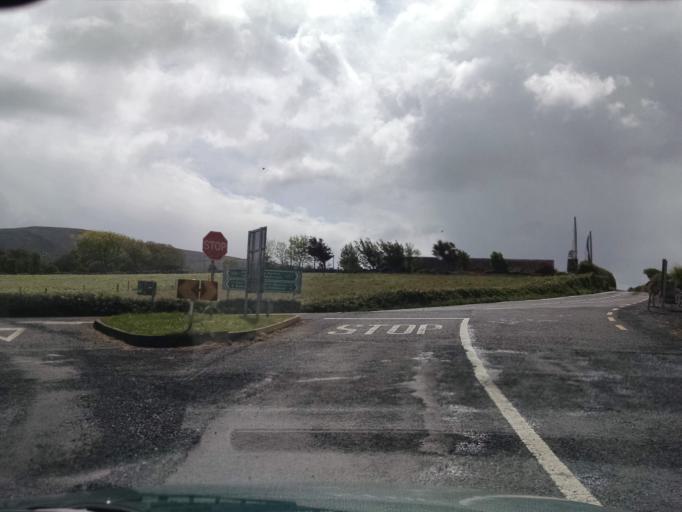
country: IE
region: Connaught
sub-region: County Galway
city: Bearna
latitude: 53.1470
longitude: -9.0805
